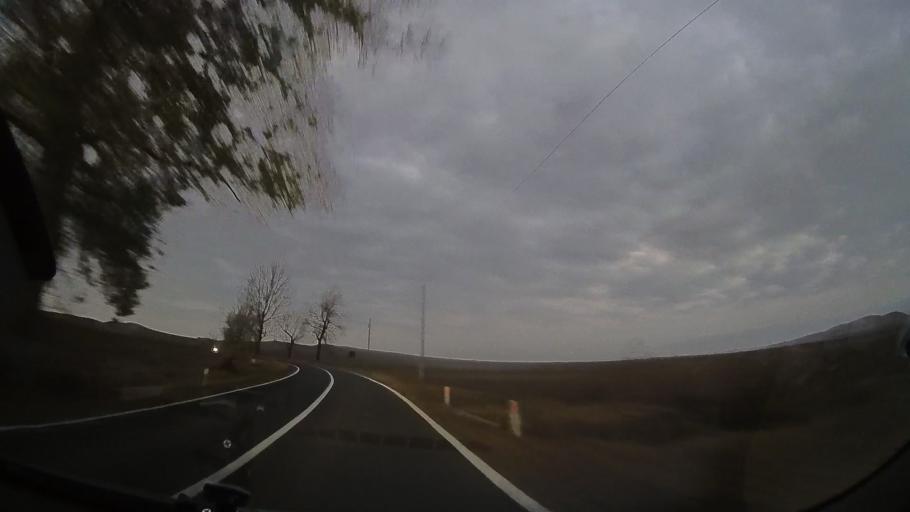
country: RO
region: Tulcea
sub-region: Comuna Nalbant
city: Nicolae Balcescu
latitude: 45.0022
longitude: 28.5959
